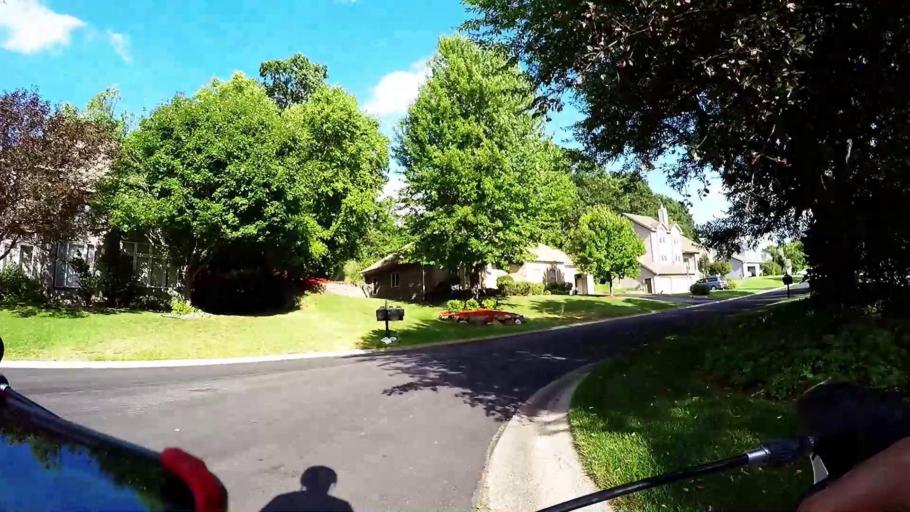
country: US
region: Minnesota
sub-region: Hennepin County
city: Eden Prairie
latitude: 44.8859
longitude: -93.4445
